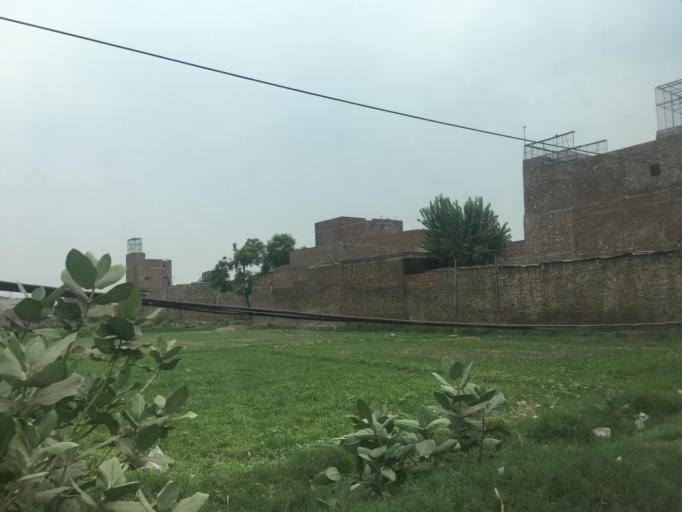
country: PK
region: Punjab
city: Lahore
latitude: 31.6167
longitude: 74.3675
